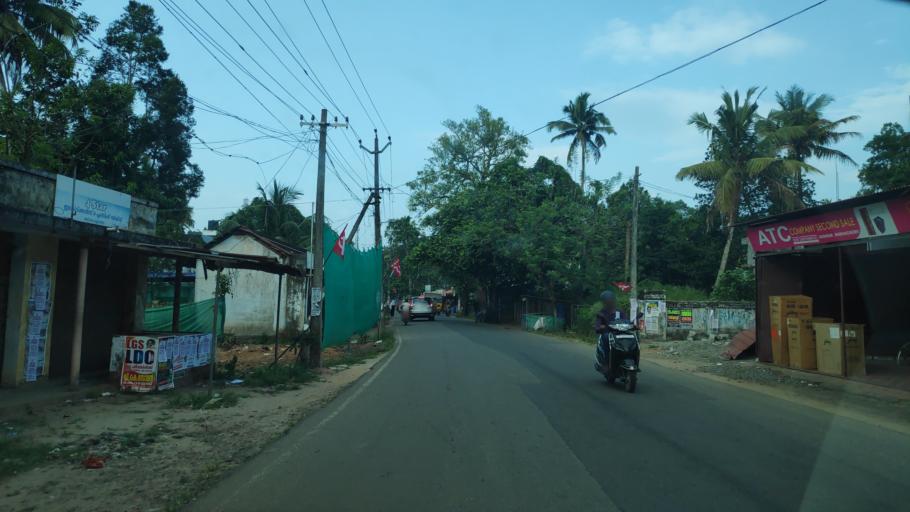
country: IN
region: Kerala
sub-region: Alappuzha
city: Alleppey
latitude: 9.5678
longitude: 76.3478
